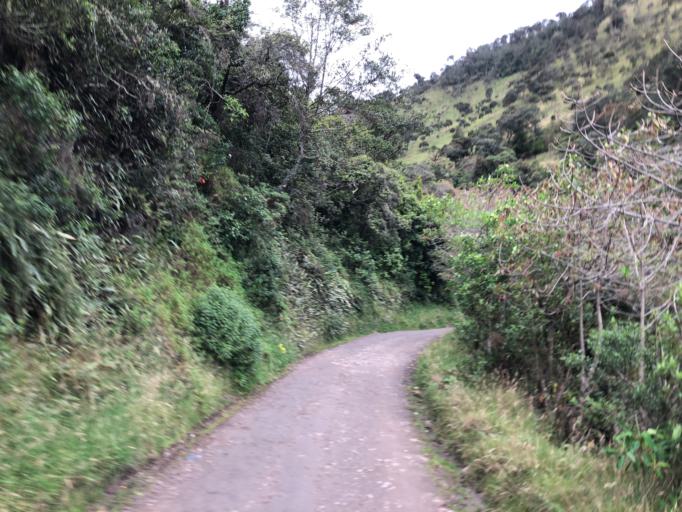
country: CO
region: Cauca
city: Totoro
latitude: 2.5087
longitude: -76.3611
